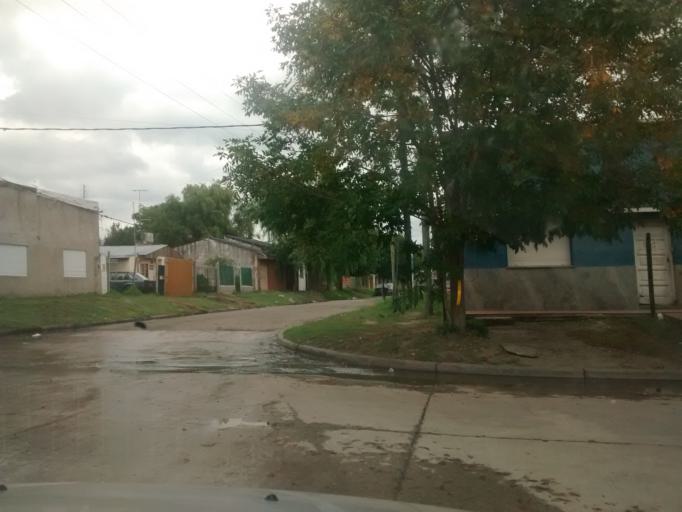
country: AR
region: Buenos Aires
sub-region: Partido de La Plata
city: La Plata
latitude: -34.9605
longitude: -57.9532
